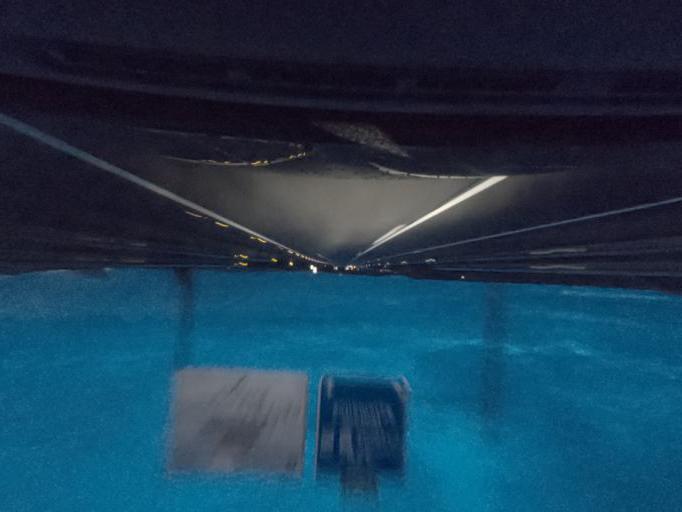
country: ES
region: Extremadura
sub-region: Provincia de Caceres
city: Caceres
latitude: 39.4281
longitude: -6.4036
